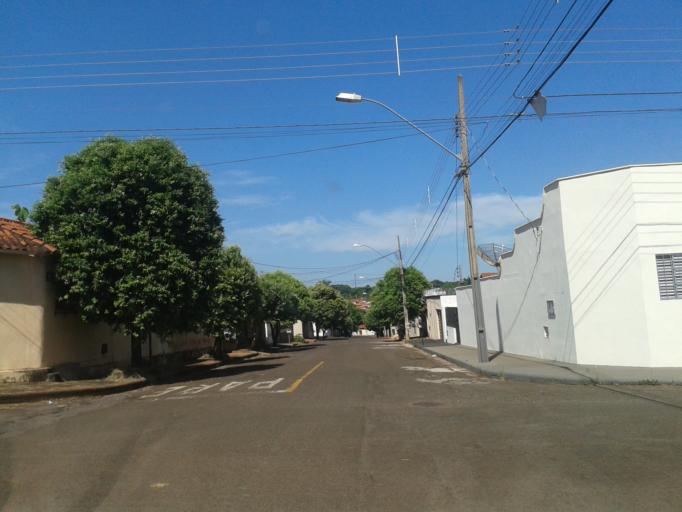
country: BR
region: Minas Gerais
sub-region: Ituiutaba
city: Ituiutaba
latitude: -18.9823
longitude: -49.4702
